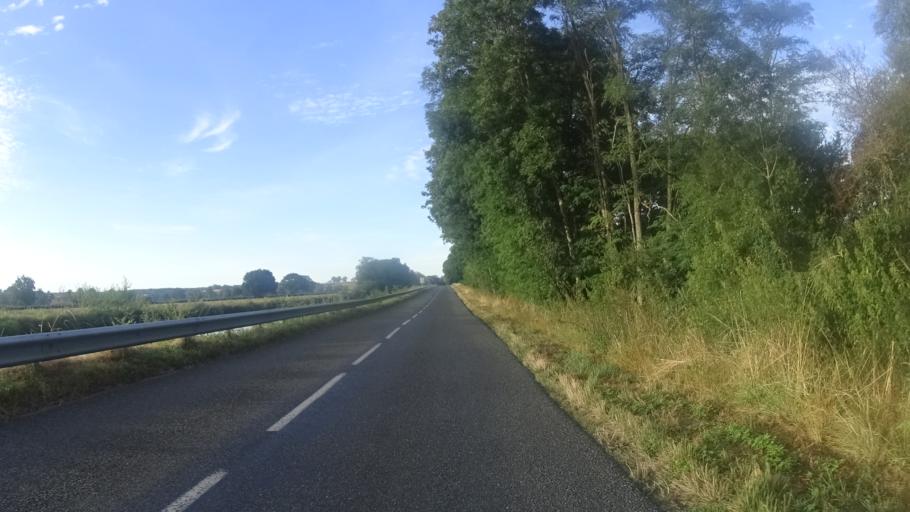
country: FR
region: Bourgogne
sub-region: Departement de Saone-et-Loire
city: Palinges
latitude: 46.5022
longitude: 4.1847
